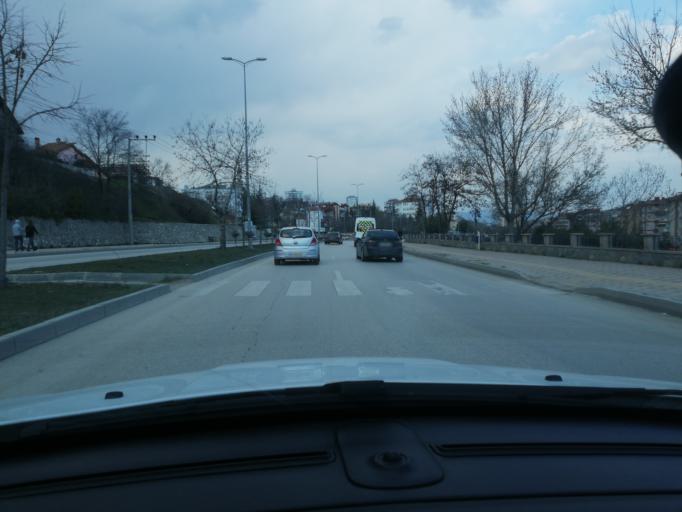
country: TR
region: Kastamonu
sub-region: Cide
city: Kastamonu
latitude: 41.3995
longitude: 33.7808
